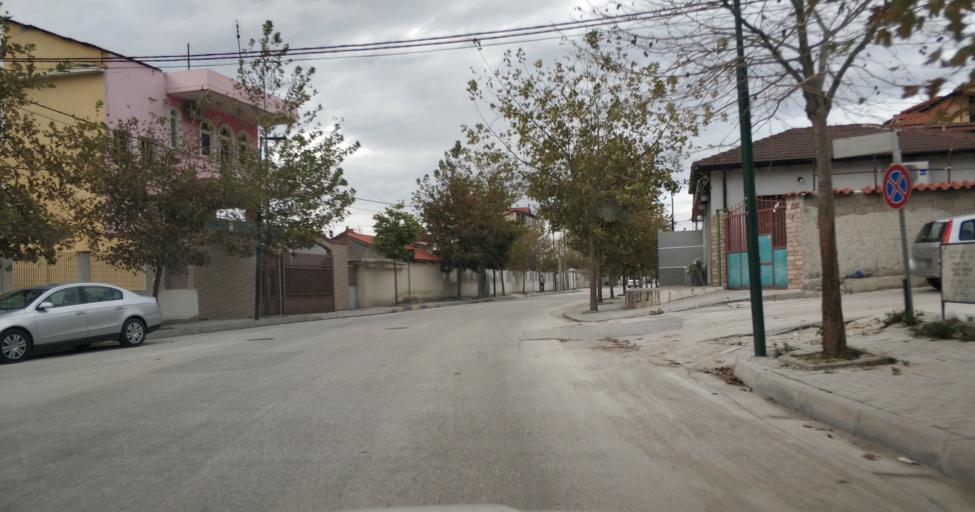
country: AL
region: Vlore
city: Vlore
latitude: 40.4469
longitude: 19.4968
